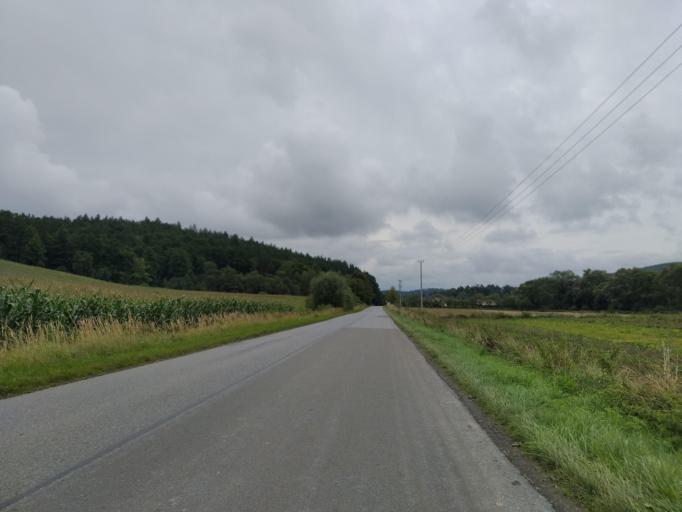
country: PL
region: Subcarpathian Voivodeship
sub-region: Powiat przemyski
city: Bircza
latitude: 49.6897
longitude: 22.3948
